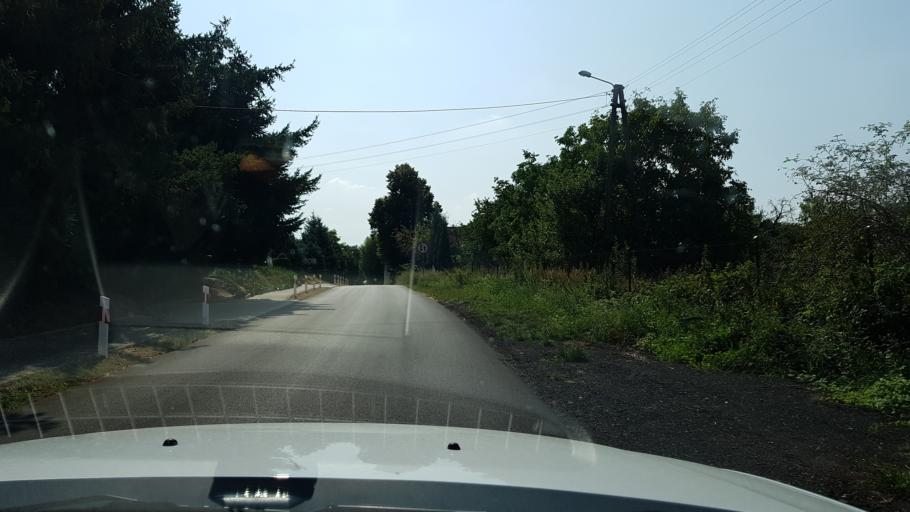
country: PL
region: West Pomeranian Voivodeship
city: Trzcinsko Zdroj
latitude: 52.9230
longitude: 14.5332
